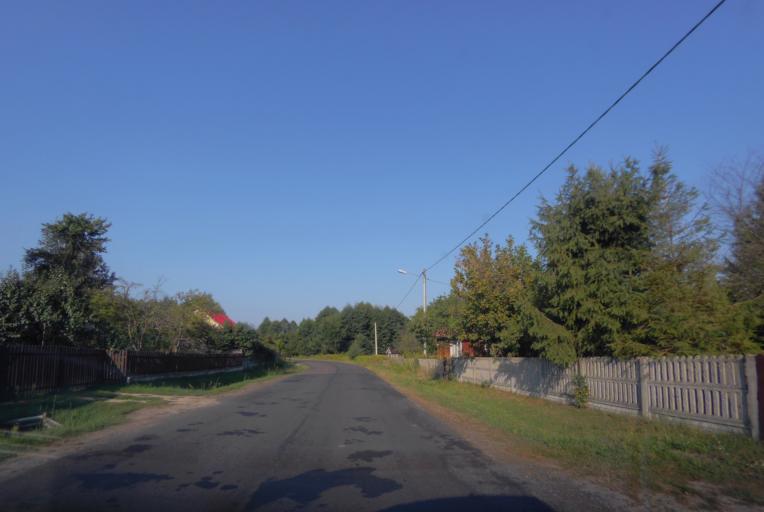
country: PL
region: Subcarpathian Voivodeship
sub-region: Powiat nizanski
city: Harasiuki
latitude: 50.5430
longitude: 22.5318
